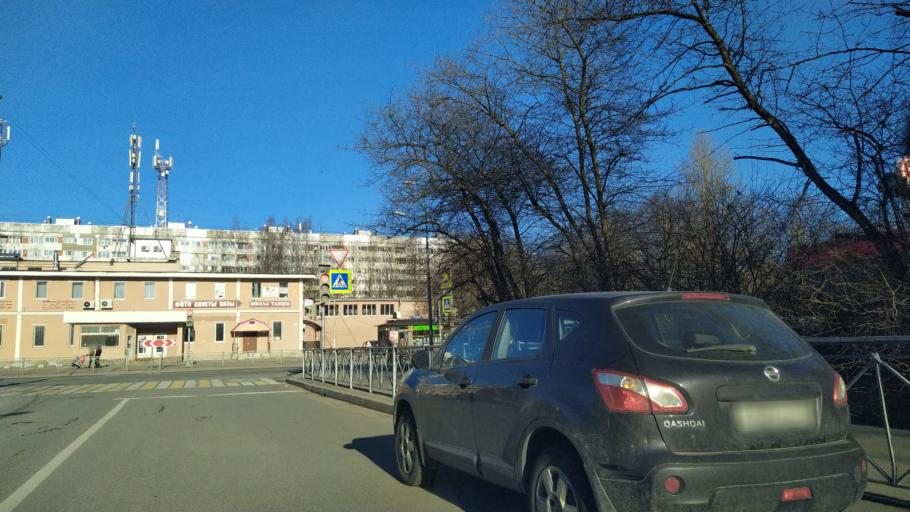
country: RU
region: St.-Petersburg
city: Grazhdanka
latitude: 60.0425
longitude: 30.4093
